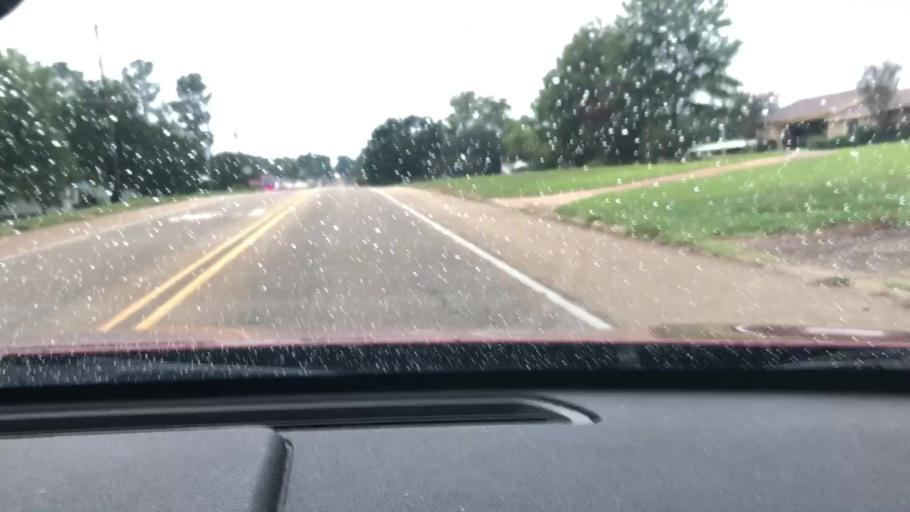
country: US
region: Arkansas
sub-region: Lafayette County
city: Stamps
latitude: 33.3650
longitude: -93.4818
